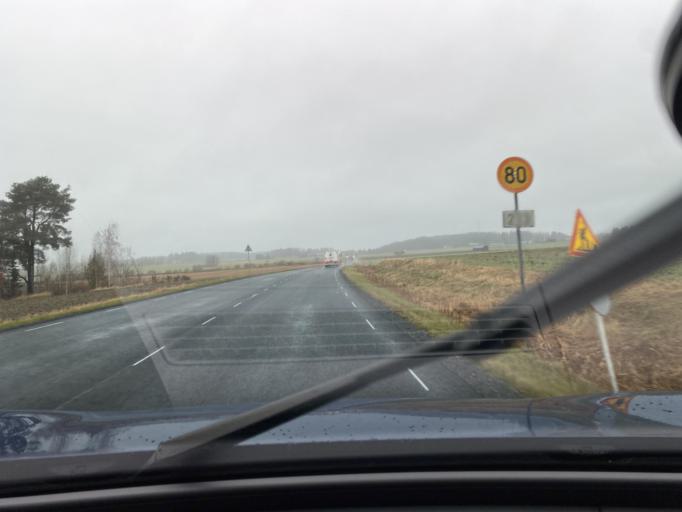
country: FI
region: Haeme
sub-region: Forssa
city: Ypaejae
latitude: 60.7876
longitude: 23.2934
